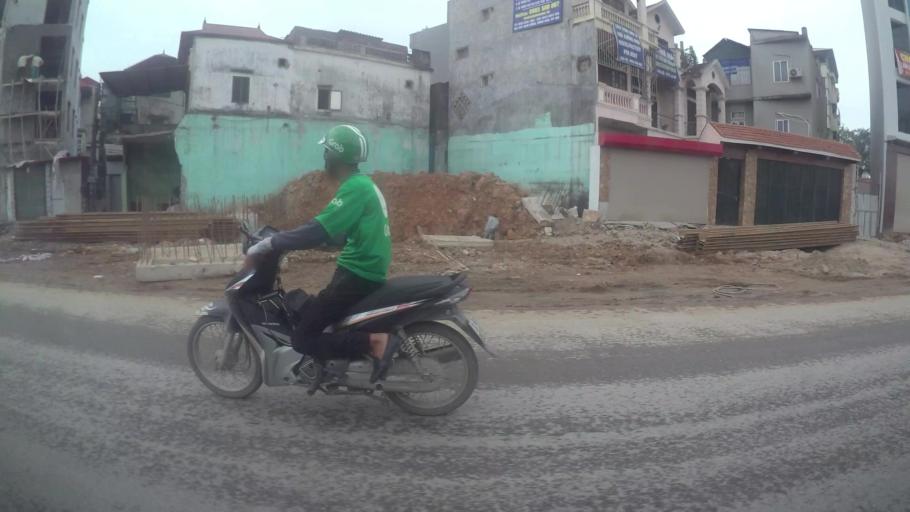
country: VN
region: Ha Noi
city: Cau Dien
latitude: 21.0608
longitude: 105.7833
